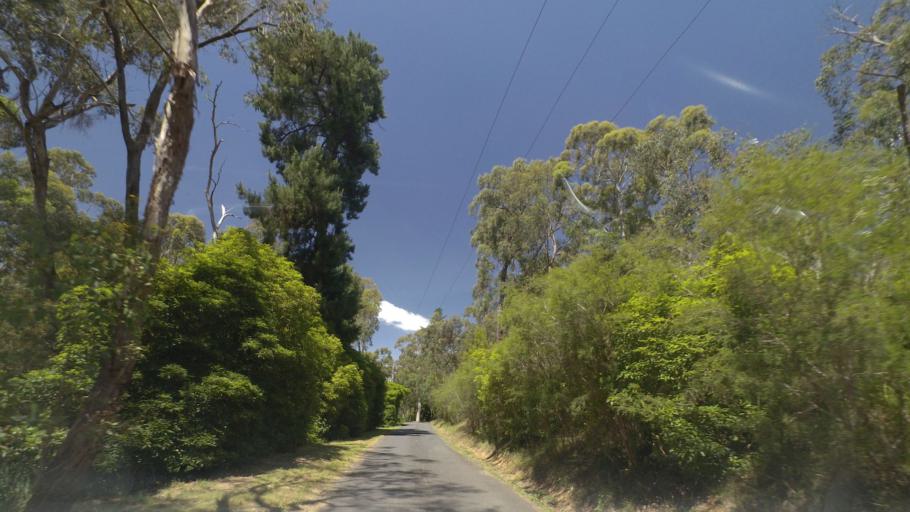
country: AU
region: Victoria
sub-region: Yarra Ranges
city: Chirnside Park
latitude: -37.7514
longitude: 145.2851
